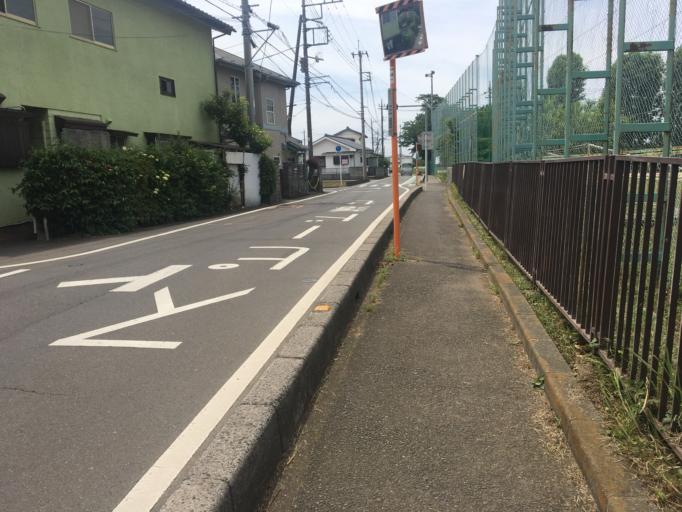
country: JP
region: Saitama
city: Sayama
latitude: 35.8388
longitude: 139.4212
